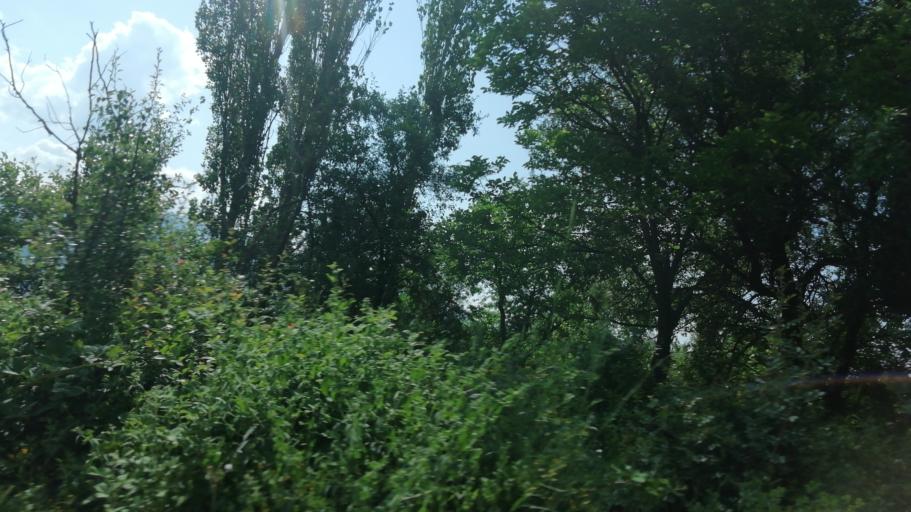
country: TR
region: Karabuk
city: Karabuk
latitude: 41.1252
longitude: 32.5776
